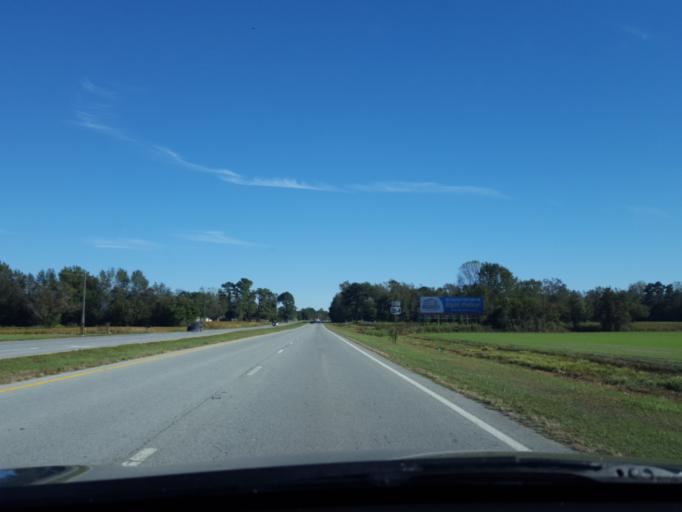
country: US
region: North Carolina
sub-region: Beaufort County
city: Washington
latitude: 35.6214
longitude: -77.1723
